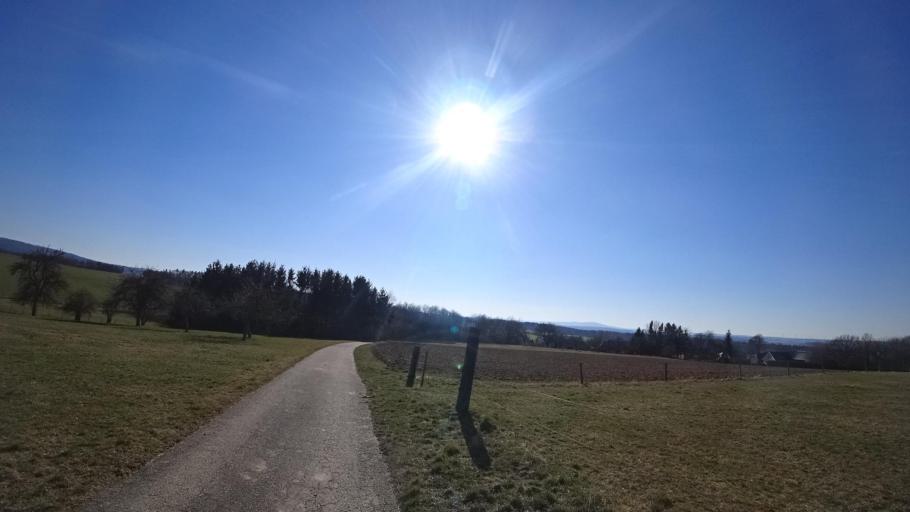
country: DE
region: Rheinland-Pfalz
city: Holzbach
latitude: 49.9553
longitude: 7.5374
